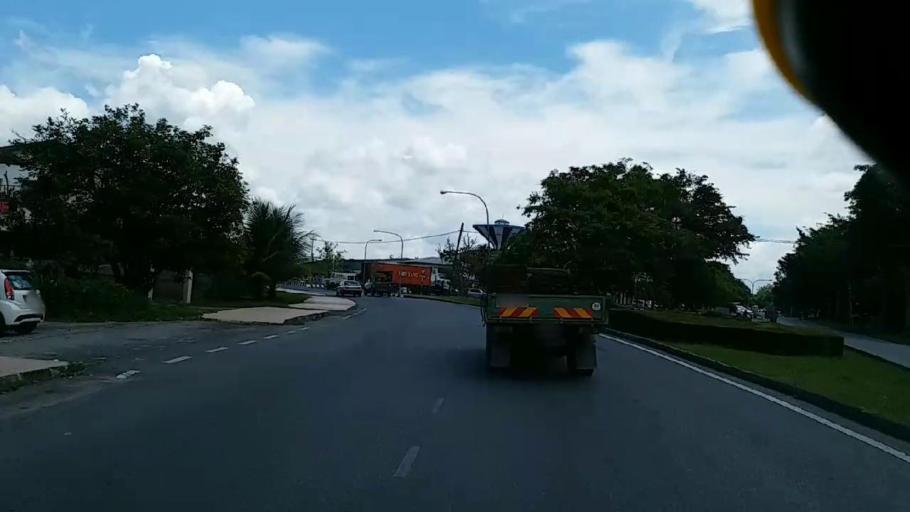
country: MY
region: Sarawak
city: Sibu
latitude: 2.3002
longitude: 111.8373
